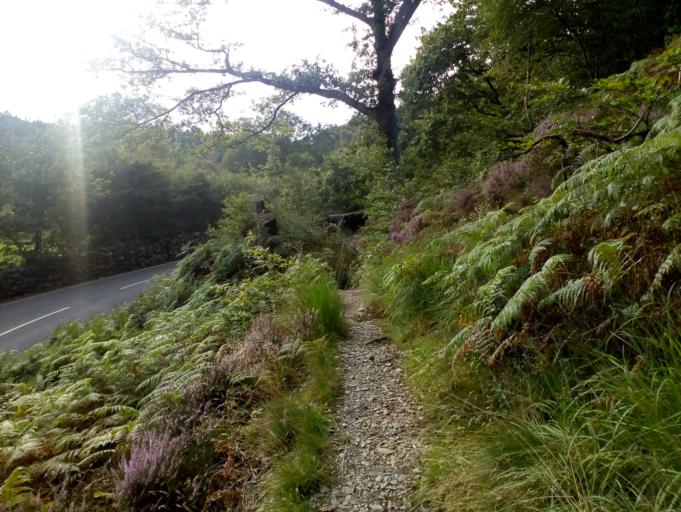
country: GB
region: Wales
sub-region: Gwynedd
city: Maentwrog
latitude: 52.9523
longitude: -4.0070
